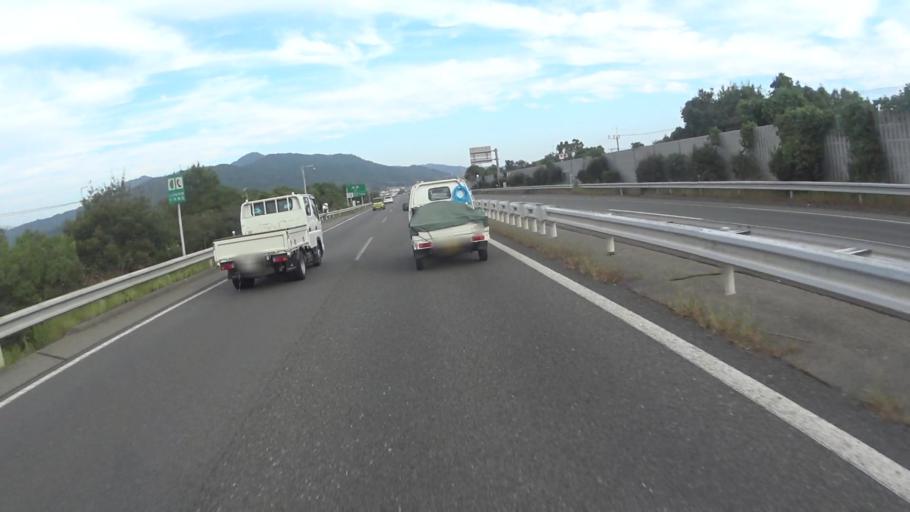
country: JP
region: Kyoto
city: Kameoka
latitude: 35.0190
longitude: 135.5529
